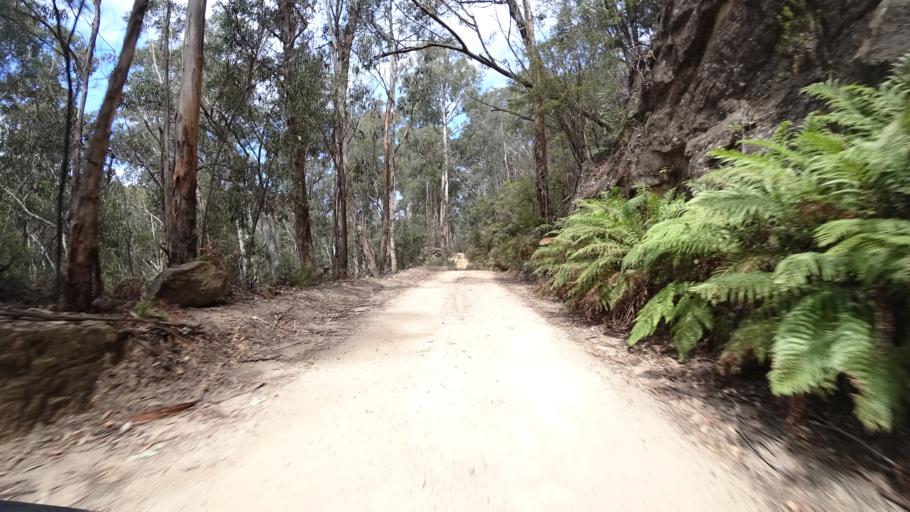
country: AU
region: New South Wales
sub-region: Lithgow
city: Lithgow
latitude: -33.2486
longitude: 150.2222
